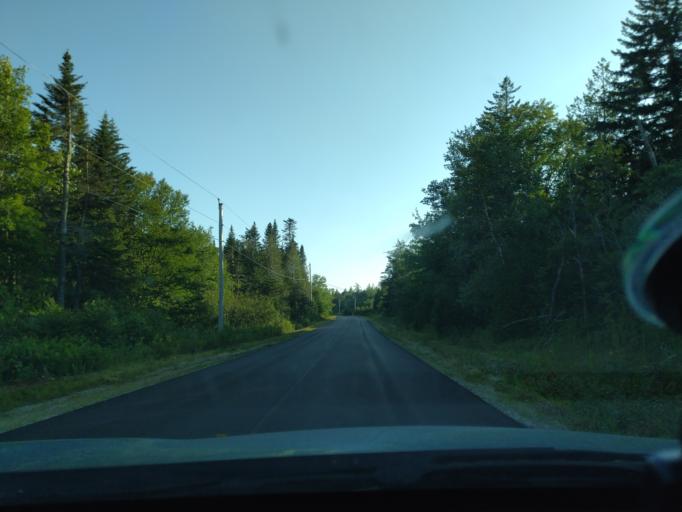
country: US
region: Maine
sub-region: Washington County
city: East Machias
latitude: 44.6957
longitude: -67.1617
